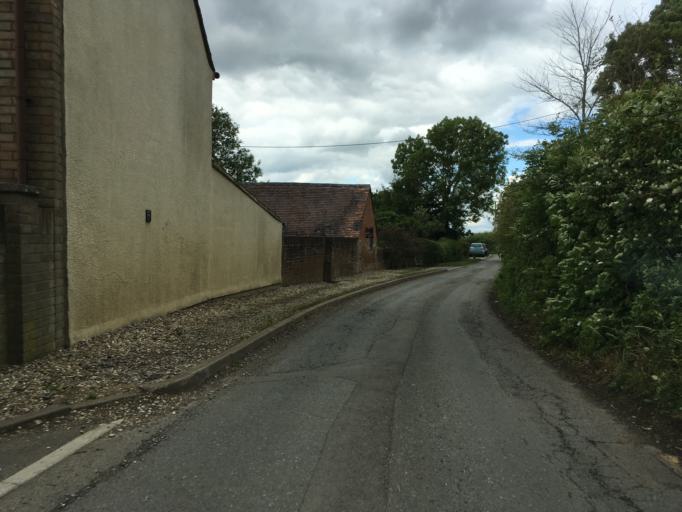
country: GB
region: England
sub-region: Gloucestershire
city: Cinderford
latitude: 51.7900
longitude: -2.3951
